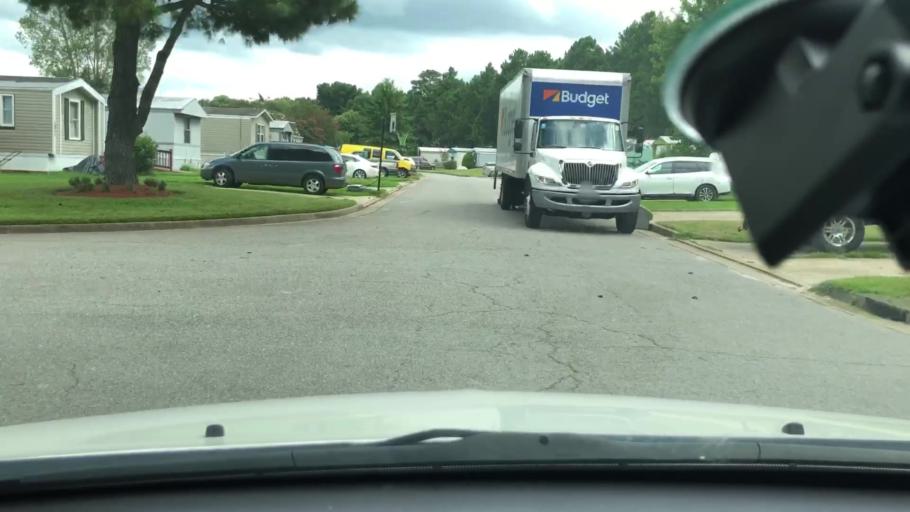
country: US
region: Virginia
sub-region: City of Chesapeake
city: Chesapeake
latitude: 36.7779
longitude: -76.2792
